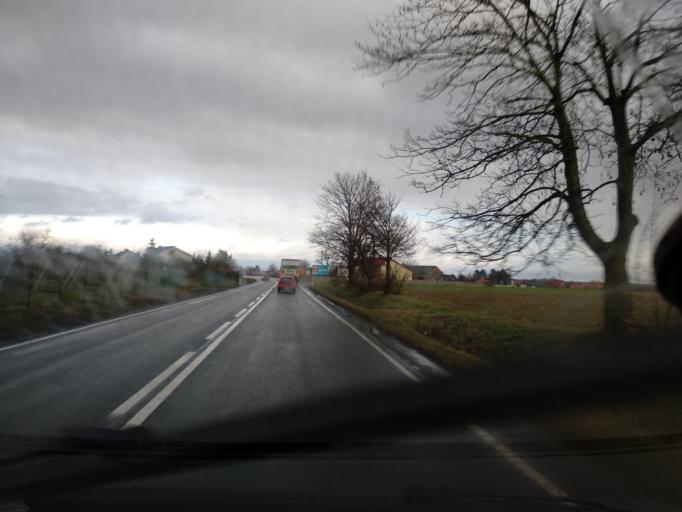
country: PL
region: Greater Poland Voivodeship
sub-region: Powiat koninski
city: Stare Miasto
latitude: 52.1513
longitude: 18.2033
